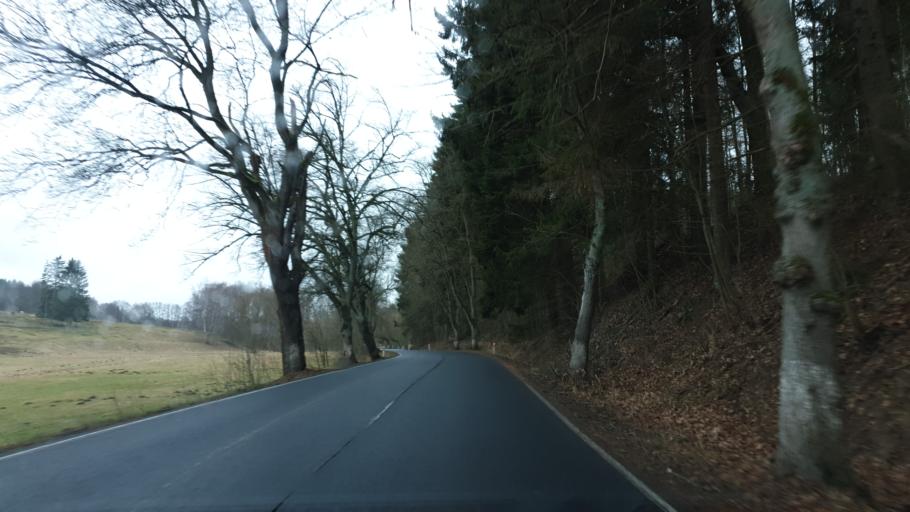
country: CZ
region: Karlovarsky
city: As
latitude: 50.2524
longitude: 12.1992
